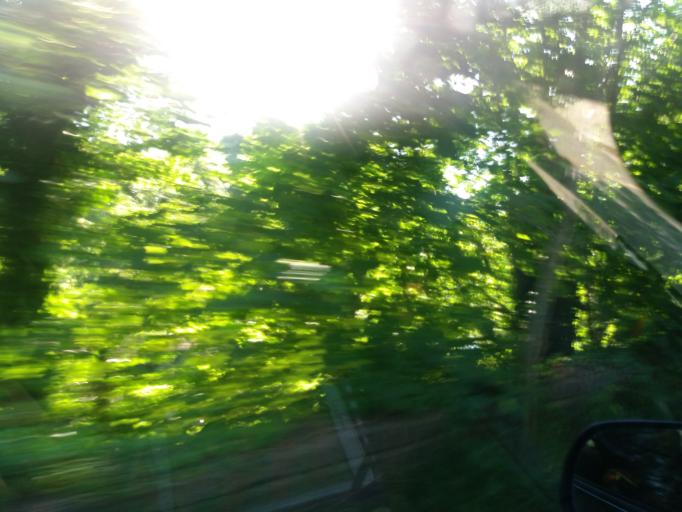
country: IE
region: Leinster
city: Hartstown
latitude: 53.3663
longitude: -6.4107
